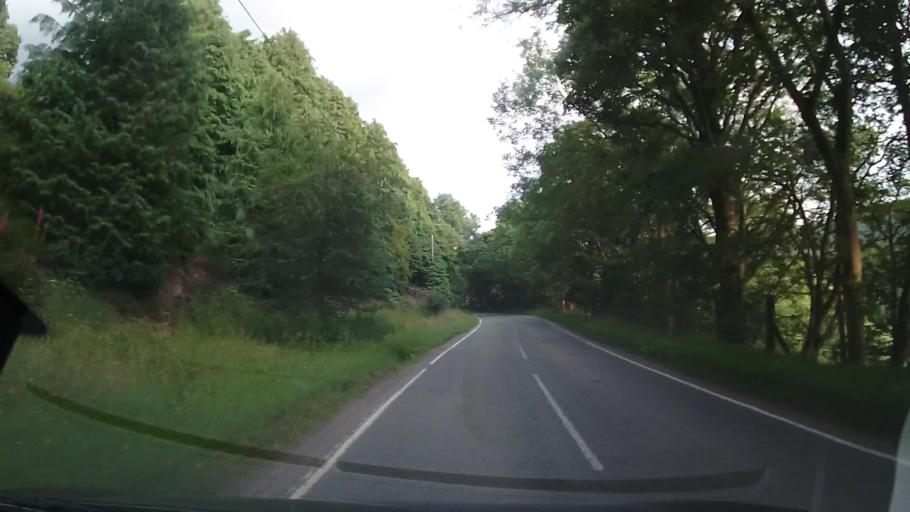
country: GB
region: Wales
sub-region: Sir Powys
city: Llangynog
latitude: 52.8481
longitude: -3.4304
